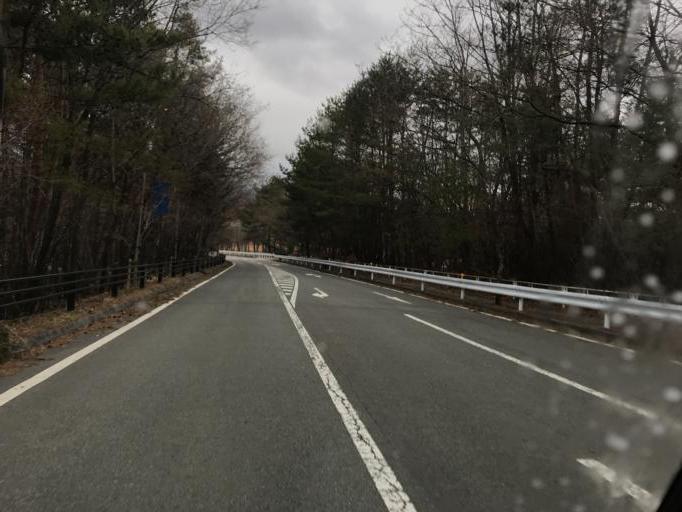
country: JP
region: Nagano
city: Chino
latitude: 35.8910
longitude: 138.3251
